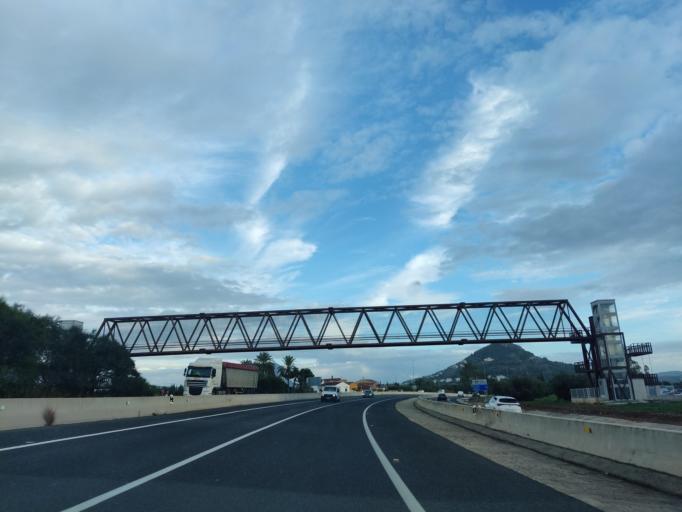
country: ES
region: Valencia
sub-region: Provincia de Alicante
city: Ondara
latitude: 38.8195
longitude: 0.0228
